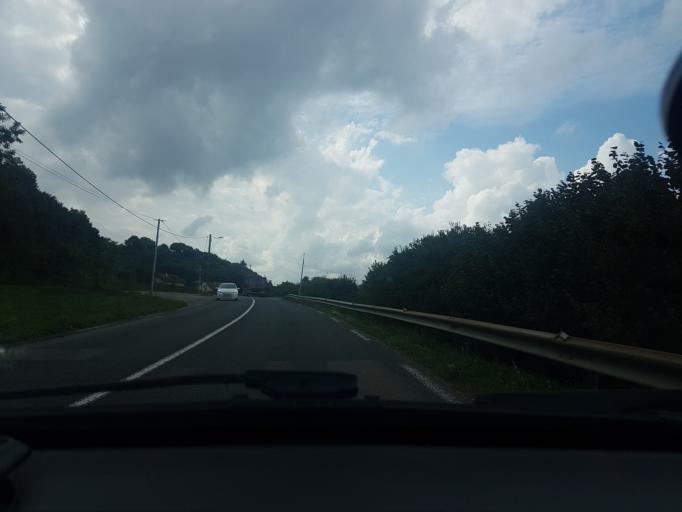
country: FR
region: Franche-Comte
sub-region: Departement du Doubs
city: Arcey
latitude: 47.5882
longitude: 6.6908
